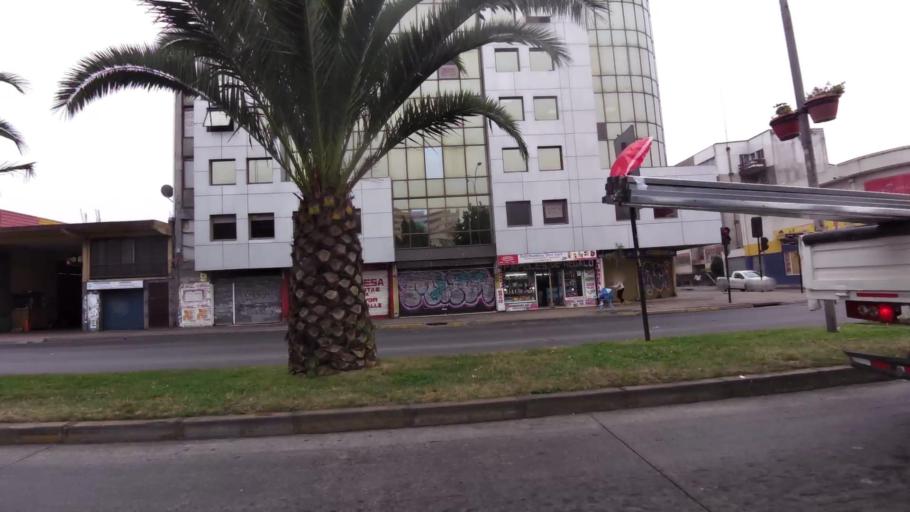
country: CL
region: Biobio
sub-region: Provincia de Concepcion
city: Concepcion
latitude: -36.8234
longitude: -73.0521
